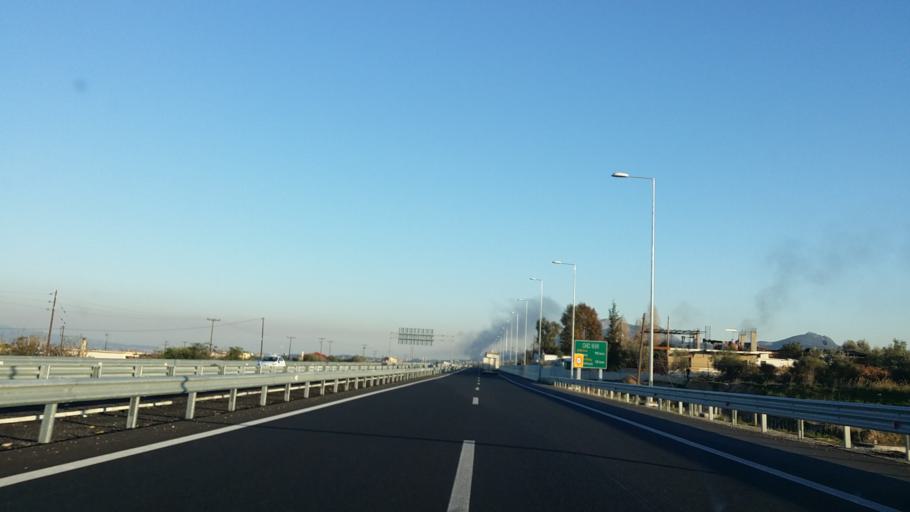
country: GR
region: Peloponnese
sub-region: Nomos Korinthias
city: Zevgolateio
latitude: 37.9254
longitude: 22.7971
